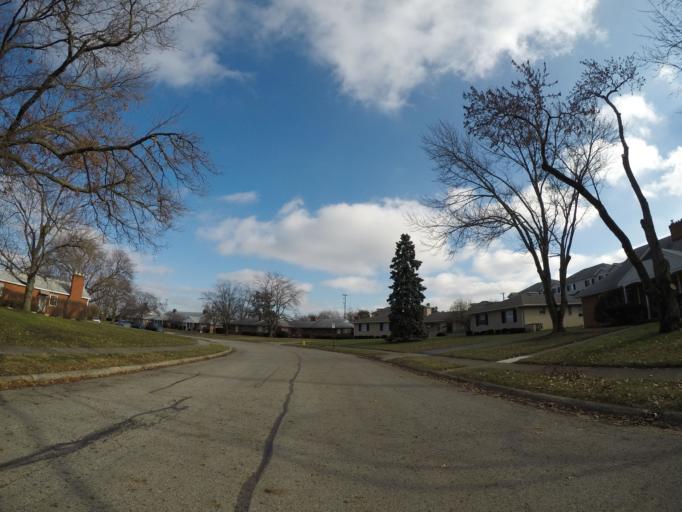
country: US
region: Ohio
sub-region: Franklin County
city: Upper Arlington
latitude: 40.0235
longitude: -83.0610
